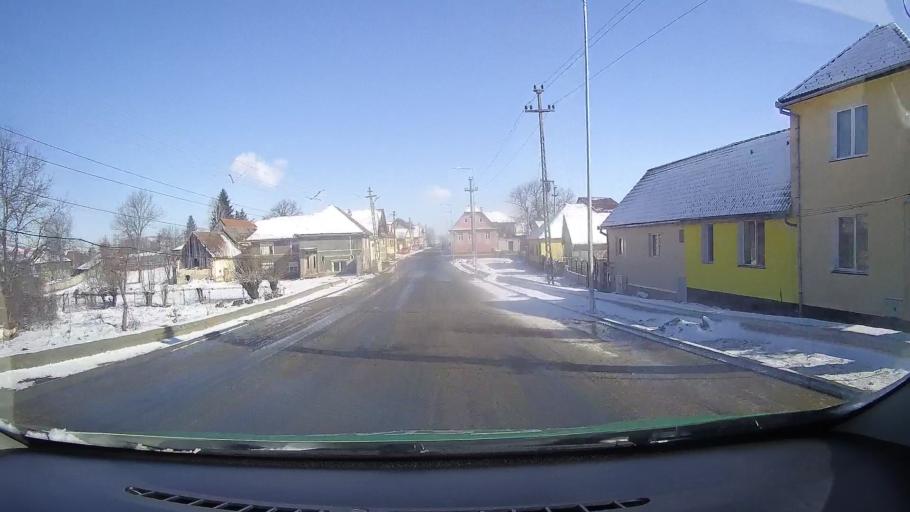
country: RO
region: Sibiu
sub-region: Comuna Avrig
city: Avrig
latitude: 45.7300
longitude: 24.3798
